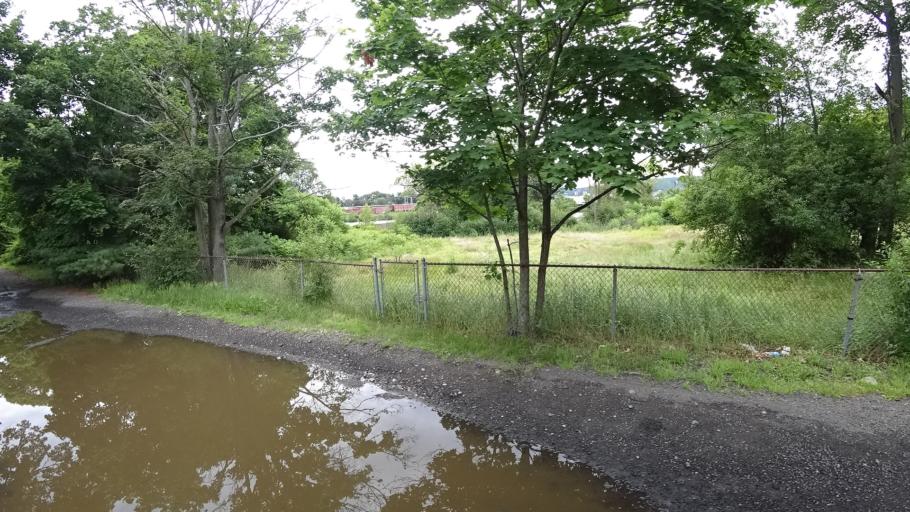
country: US
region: Massachusetts
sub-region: Norfolk County
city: Dedham
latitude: 42.2337
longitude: -71.1383
